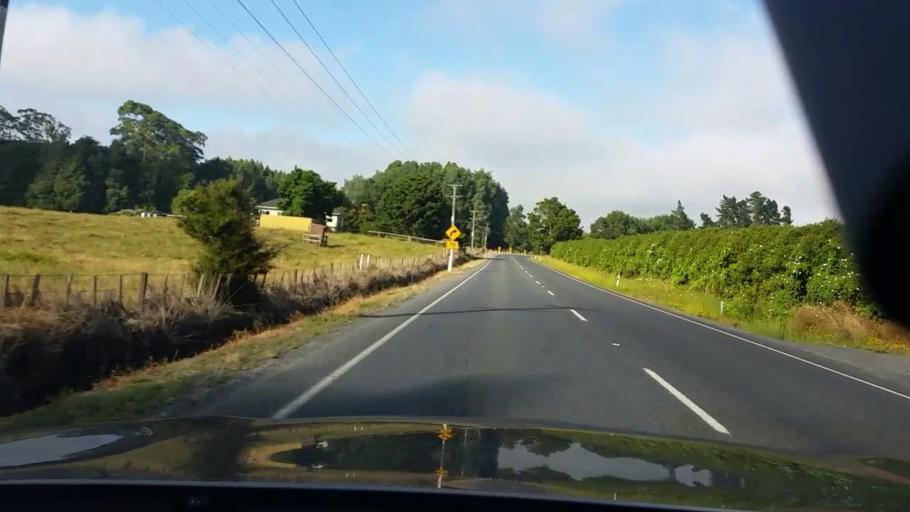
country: NZ
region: Waikato
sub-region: Hamilton City
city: Hamilton
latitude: -37.5959
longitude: 175.3594
